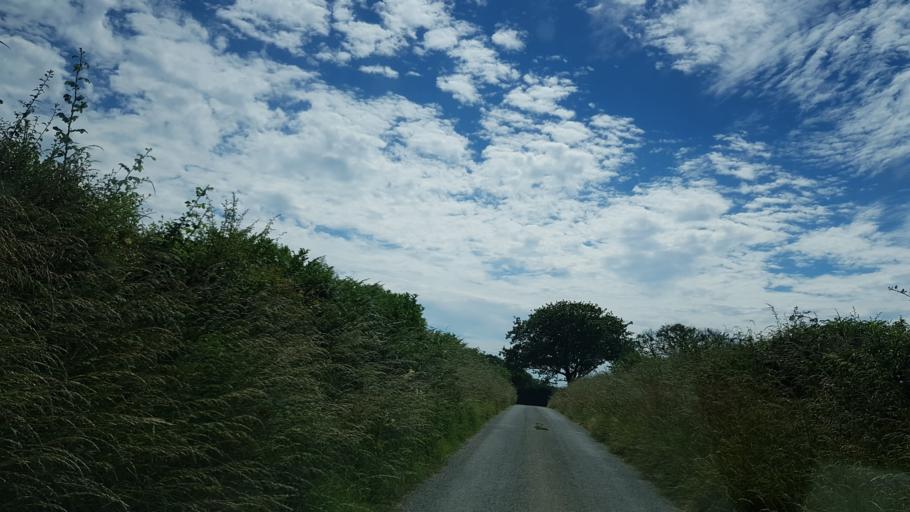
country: GB
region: Wales
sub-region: Pembrokeshire
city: Wiston
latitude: 51.8224
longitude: -4.9151
